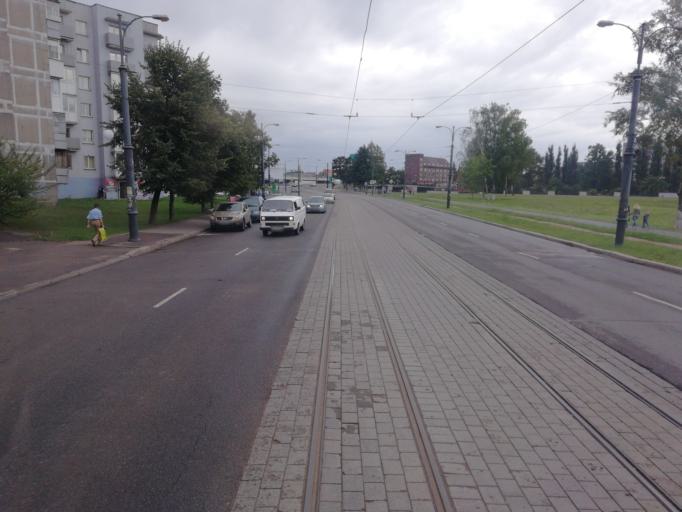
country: RU
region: Kaliningrad
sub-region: Gorod Kaliningrad
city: Kaliningrad
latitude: 54.7016
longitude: 20.5167
